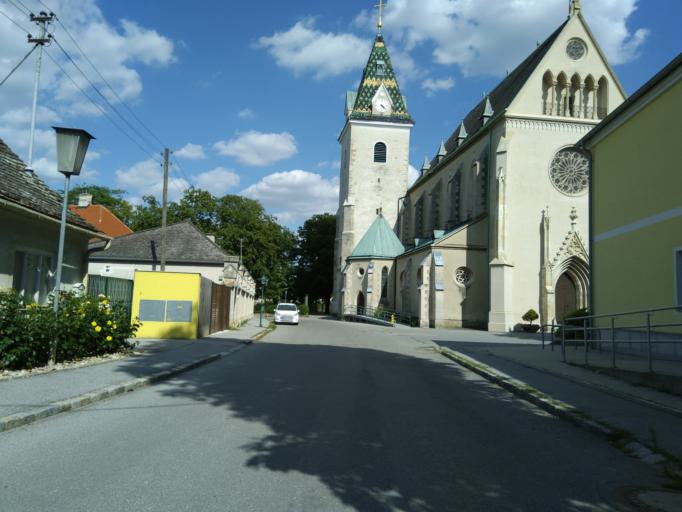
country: AT
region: Lower Austria
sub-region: Politischer Bezirk Mistelbach
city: Gross-Engersdorf
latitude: 48.3569
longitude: 16.5684
